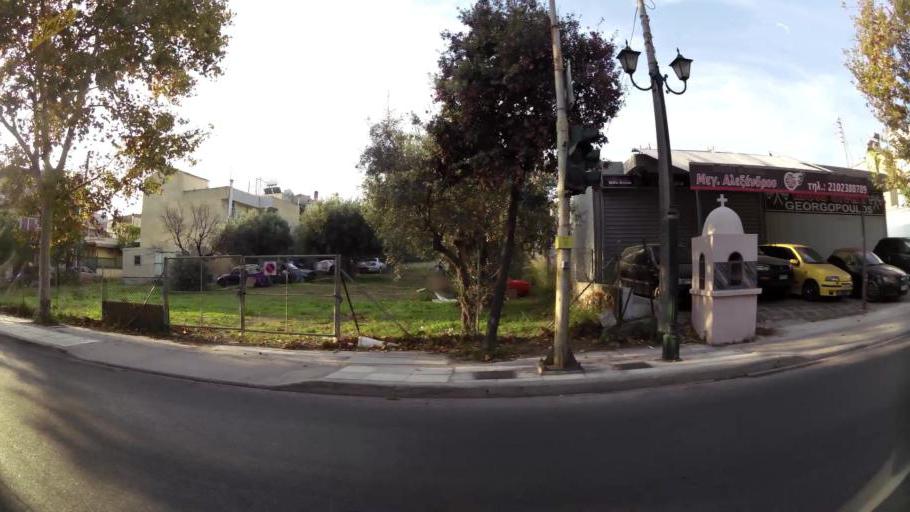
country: GR
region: Attica
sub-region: Nomarchia Dytikis Attikis
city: Zefyri
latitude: 38.0694
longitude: 23.7071
